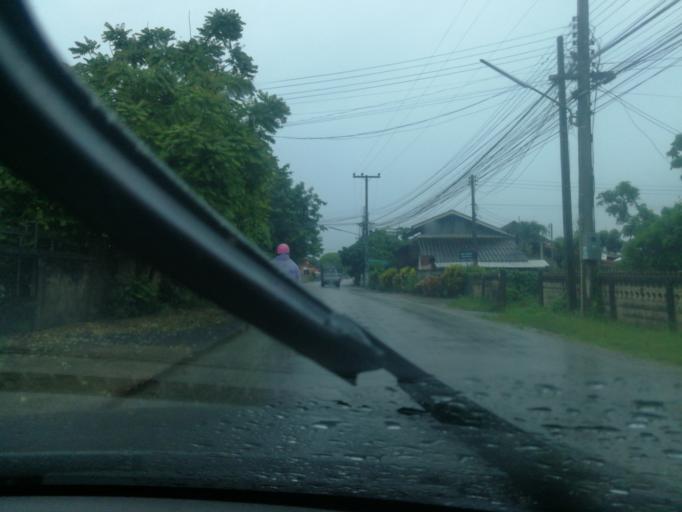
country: TH
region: Chiang Mai
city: San Pa Tong
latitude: 18.6018
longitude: 98.9095
